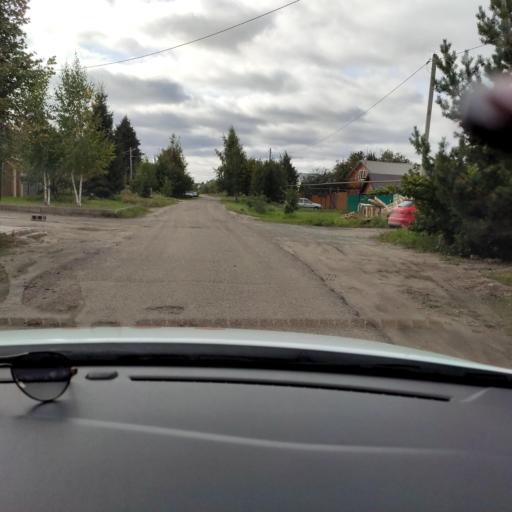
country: RU
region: Tatarstan
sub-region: Gorod Kazan'
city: Kazan
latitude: 55.7235
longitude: 49.1040
